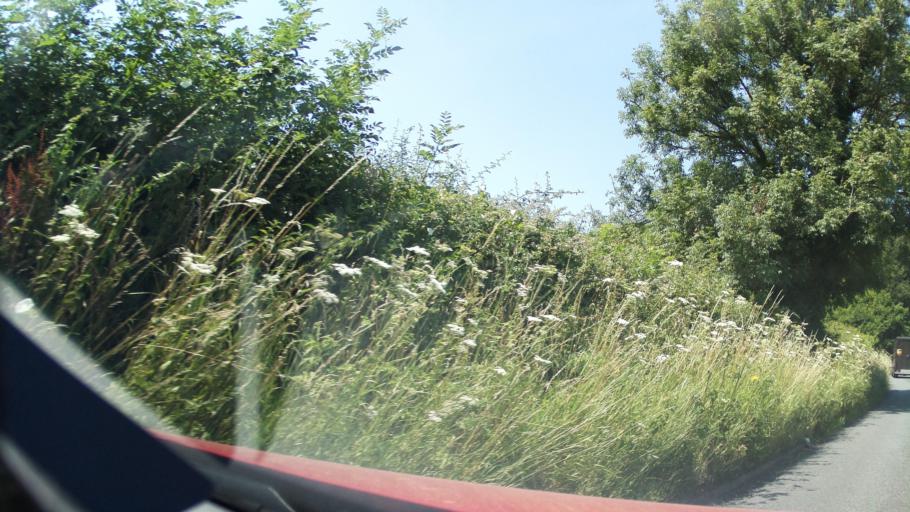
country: GB
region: Wales
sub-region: Caerphilly County Borough
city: Caerphilly
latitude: 51.5485
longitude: -3.2087
